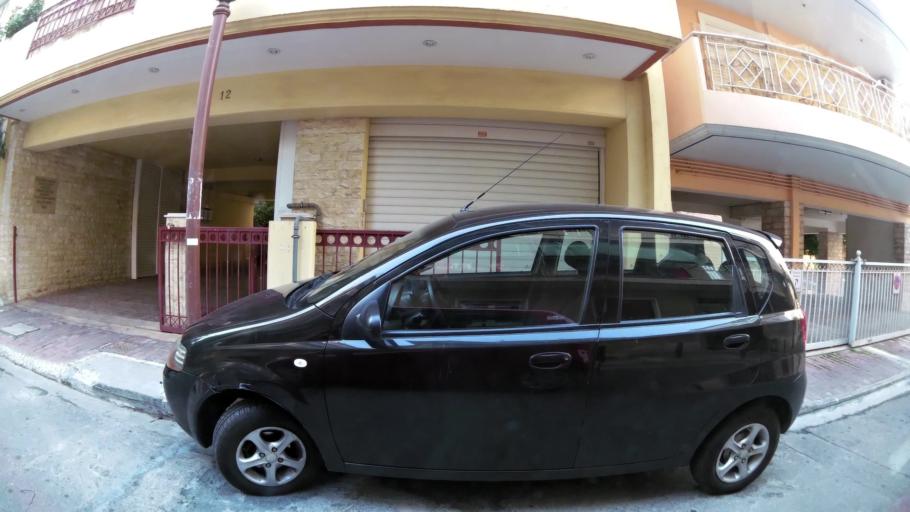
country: GR
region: Attica
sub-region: Nomarchia Athinas
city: Dhafni
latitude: 37.9547
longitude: 23.7378
